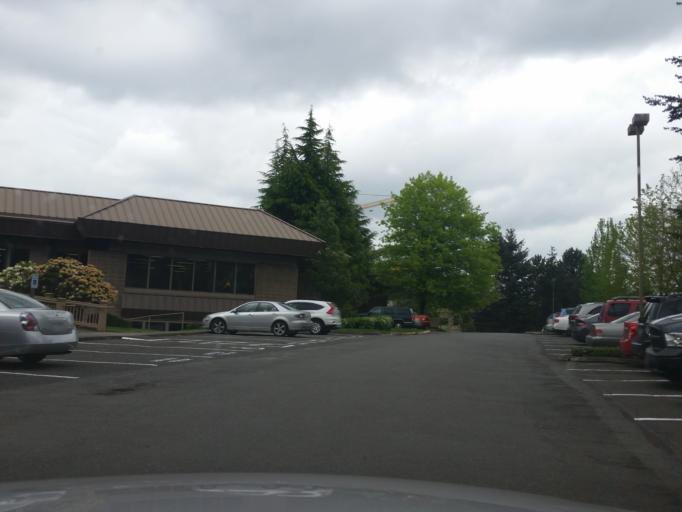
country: US
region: Washington
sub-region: King County
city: Bellevue
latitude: 47.6221
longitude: -122.1821
